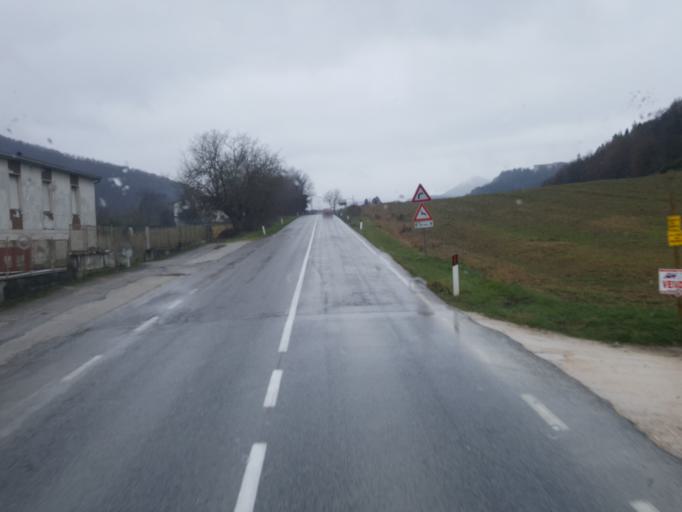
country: IT
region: The Marches
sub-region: Provincia di Ancona
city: Sassoferrato
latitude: 43.4374
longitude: 12.8815
